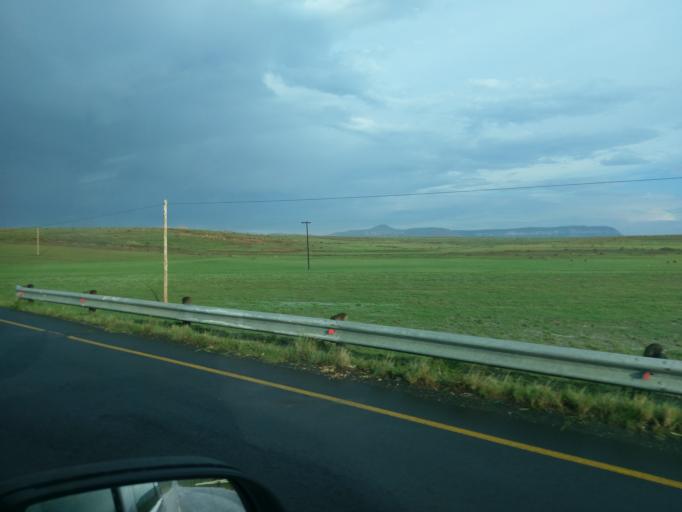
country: LS
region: Mafeteng
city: Mafeteng
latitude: -29.7639
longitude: 27.3197
